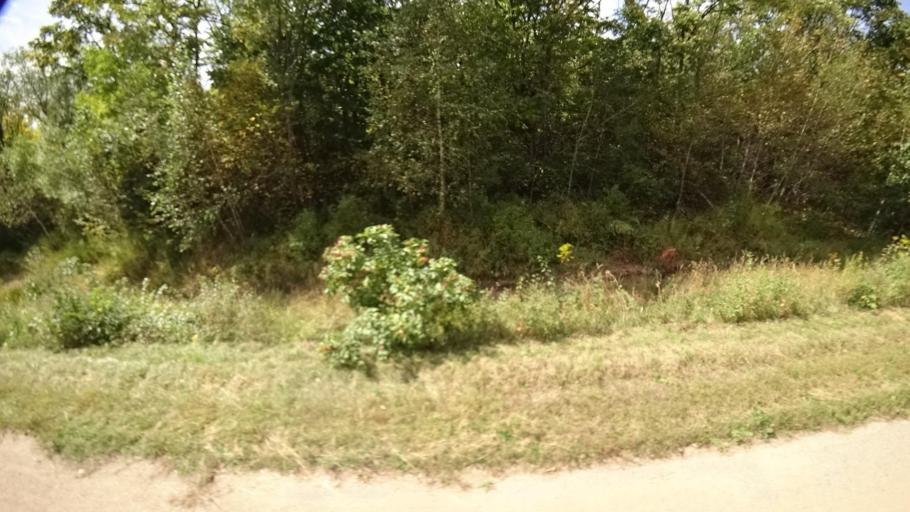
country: RU
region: Primorskiy
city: Yakovlevka
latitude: 44.6525
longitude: 133.5972
